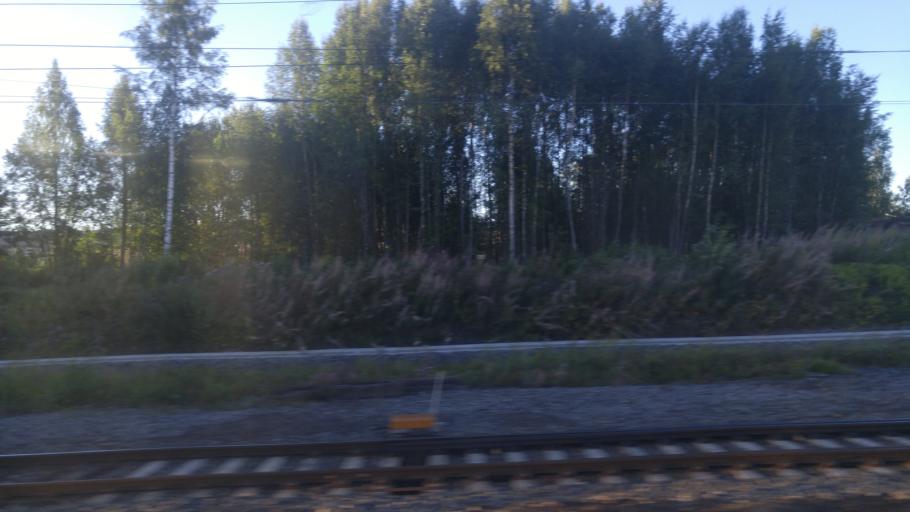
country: NO
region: Akershus
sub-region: Lorenskog
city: Kjenn
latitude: 59.9406
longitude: 10.8601
